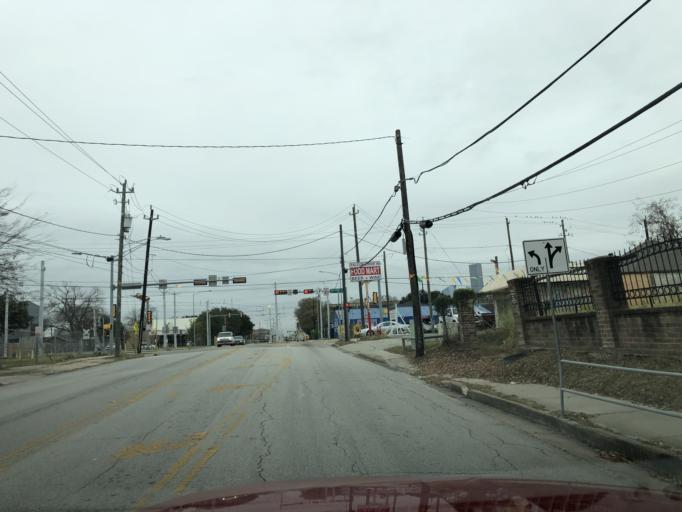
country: US
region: Texas
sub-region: Harris County
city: Houston
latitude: 29.7838
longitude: -95.3653
